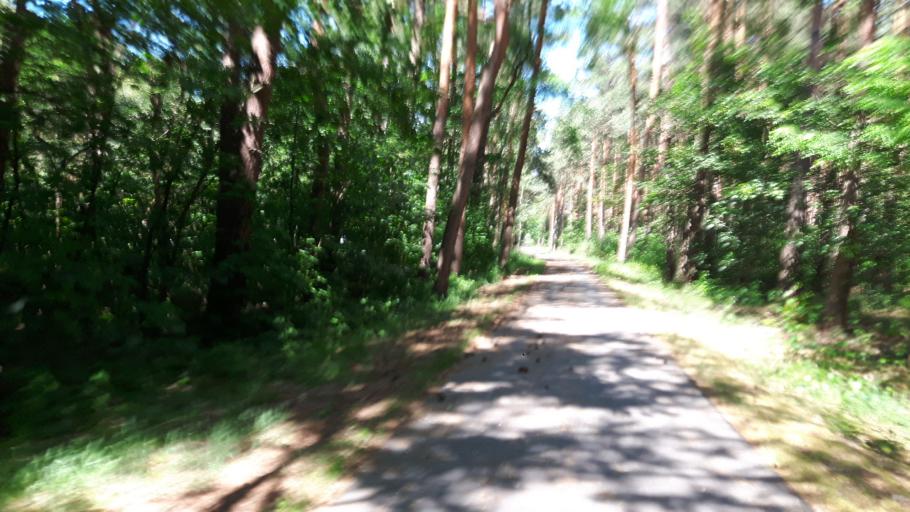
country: DE
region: Brandenburg
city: Treuenbrietzen
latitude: 52.0552
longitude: 12.8212
